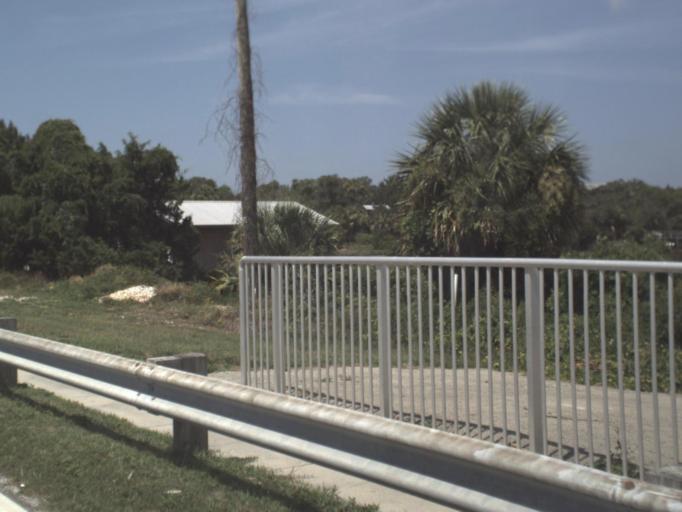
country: US
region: Florida
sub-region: Levy County
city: Chiefland
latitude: 29.1498
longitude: -83.0315
